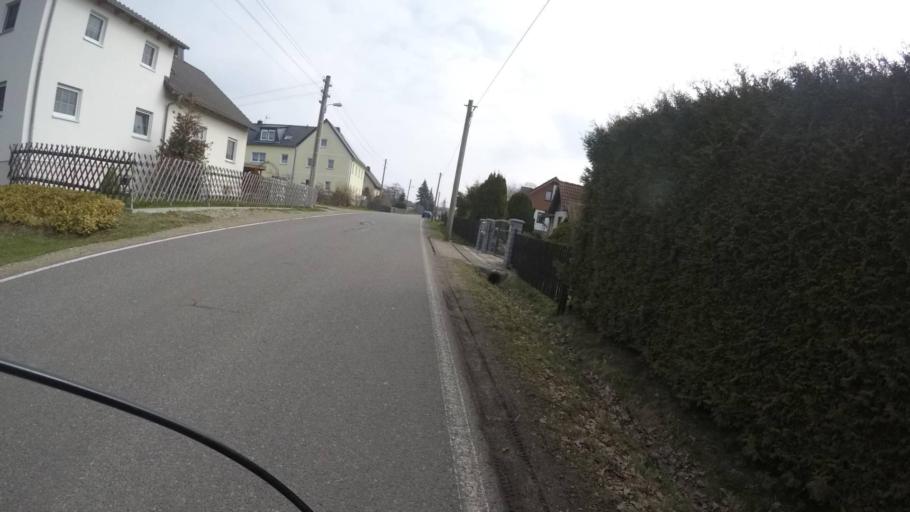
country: DE
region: Saxony
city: Niederfrohna
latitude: 50.8870
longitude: 12.6947
